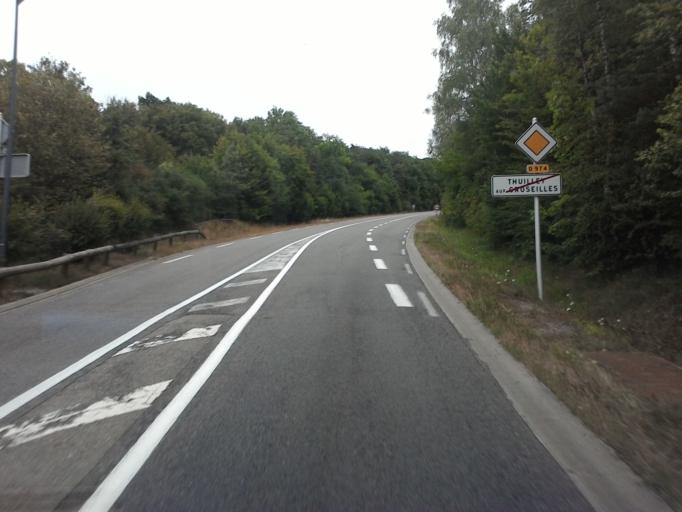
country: FR
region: Lorraine
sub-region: Departement de Meurthe-et-Moselle
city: Colombey-les-Belles
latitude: 48.5748
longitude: 5.9749
